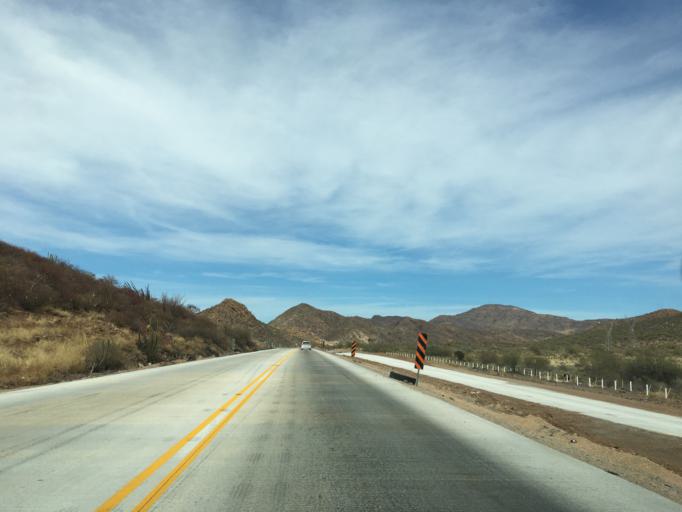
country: MX
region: Sonora
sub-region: Empalme
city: La Palma
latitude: 28.4463
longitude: -111.0465
